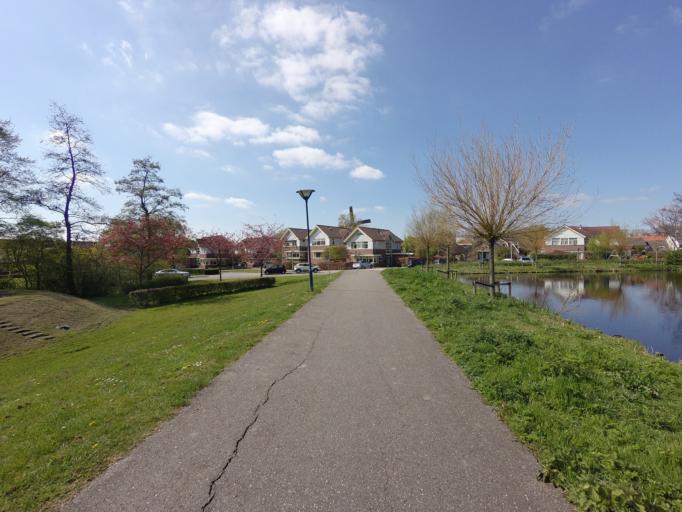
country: NL
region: South Holland
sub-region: Gemeente Zoetermeer
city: Zoetermeer
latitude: 52.0532
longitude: 4.5007
